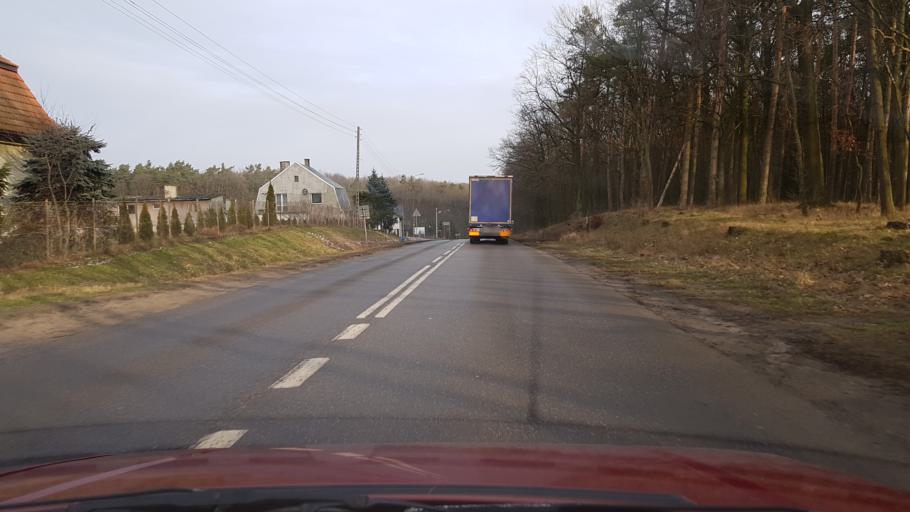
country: PL
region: West Pomeranian Voivodeship
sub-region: Powiat policki
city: Police
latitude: 53.5200
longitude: 14.5682
